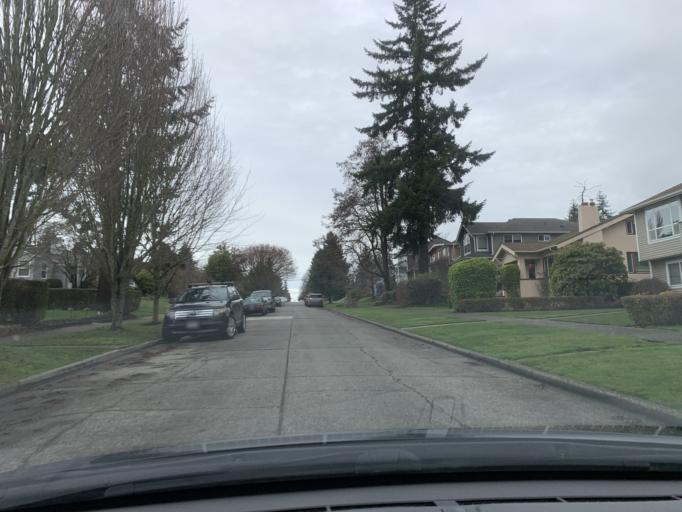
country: US
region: Washington
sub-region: King County
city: White Center
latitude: 47.5632
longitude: -122.3921
